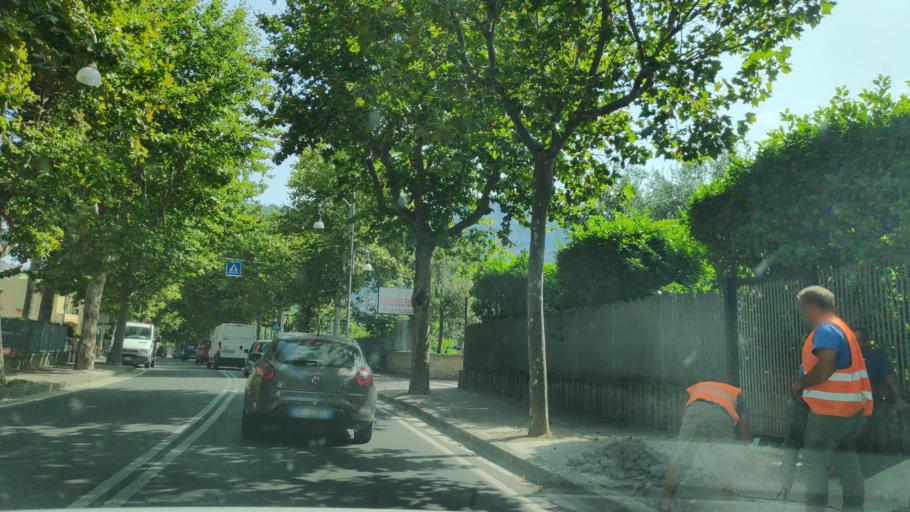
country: IT
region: Campania
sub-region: Provincia di Napoli
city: Piano di Sorrento
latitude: 40.6313
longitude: 14.4156
